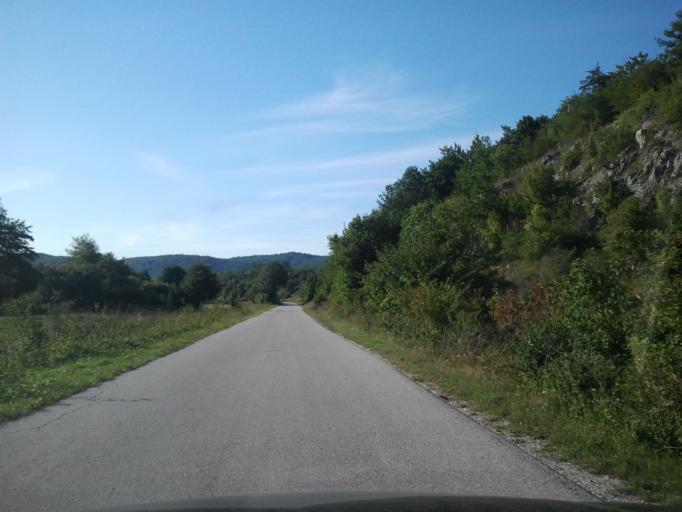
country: HR
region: Zadarska
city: Obrovac
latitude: 44.3408
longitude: 15.6434
